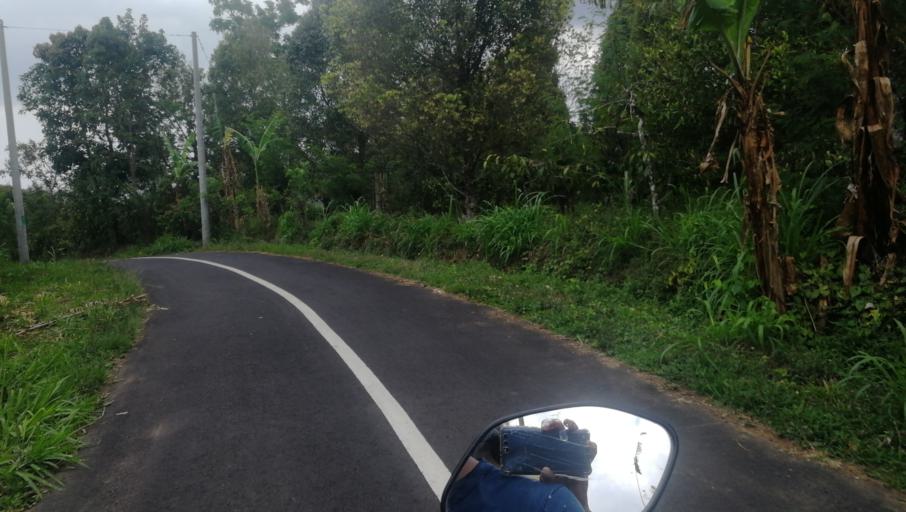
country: ID
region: Bali
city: Munduk
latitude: -8.3018
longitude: 115.0580
